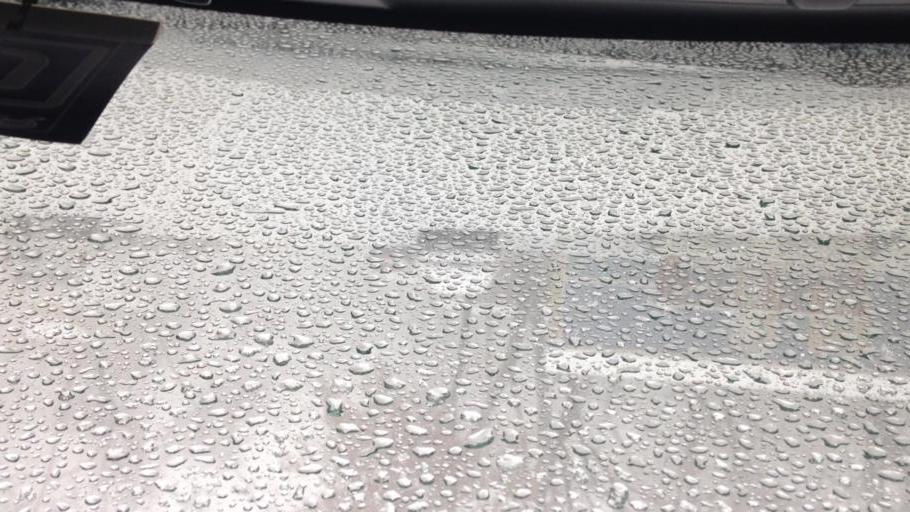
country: US
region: Kansas
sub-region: Johnson County
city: Shawnee
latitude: 39.1147
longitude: -94.7249
